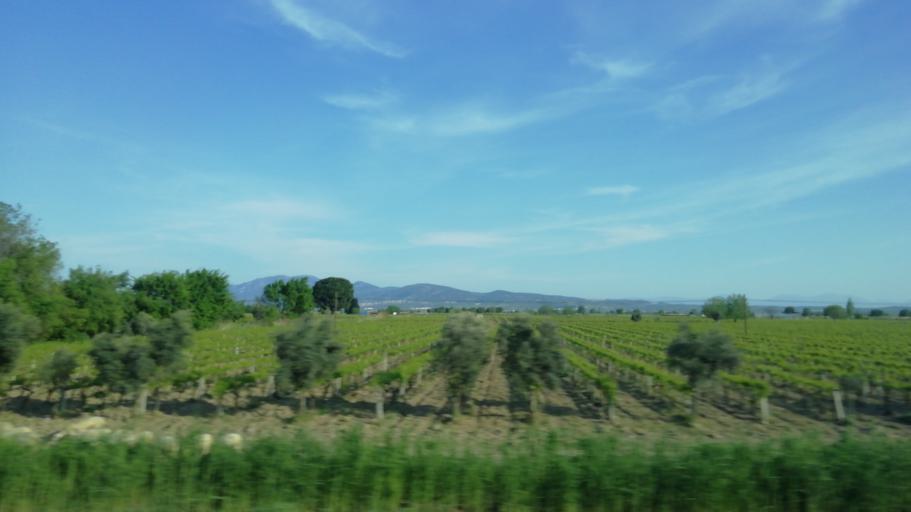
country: TR
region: Manisa
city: Saruhanli
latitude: 38.7483
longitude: 27.6182
